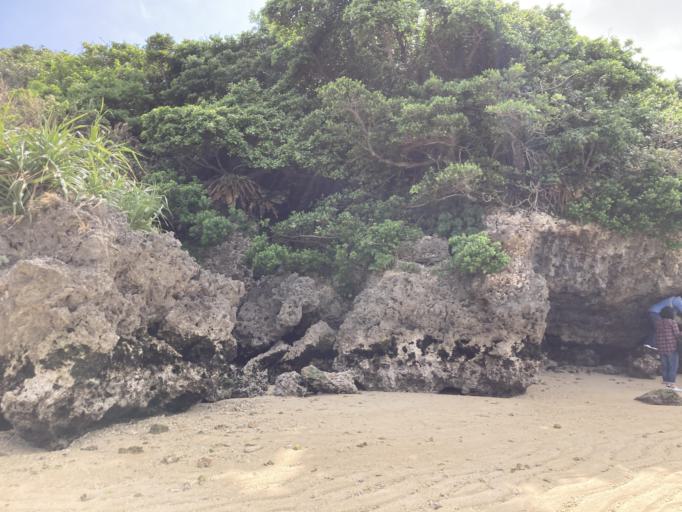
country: JP
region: Okinawa
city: Itoman
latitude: 26.1093
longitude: 127.6592
